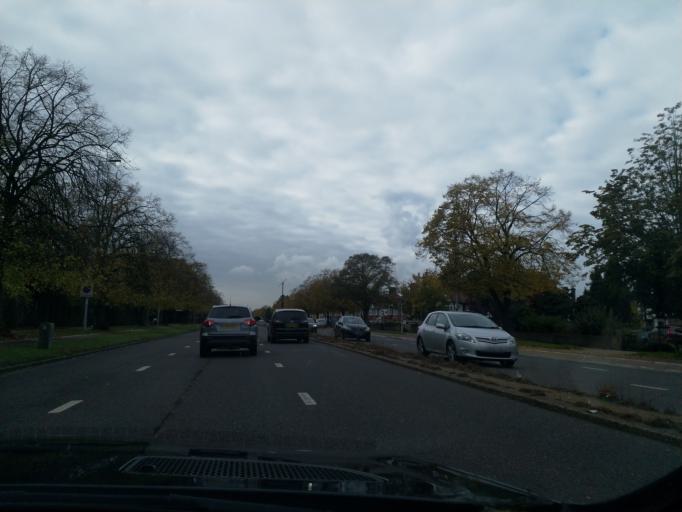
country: GB
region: England
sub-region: Greater London
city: Hounslow
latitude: 51.4770
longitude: -0.3794
